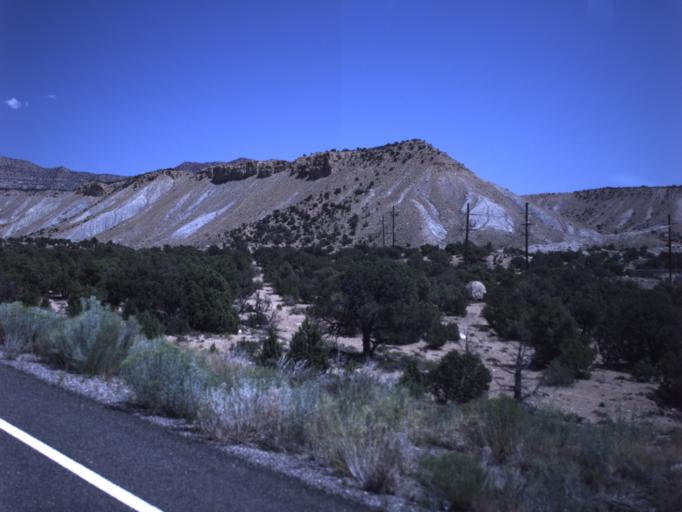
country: US
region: Utah
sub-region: Emery County
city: Orangeville
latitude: 39.2741
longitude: -111.1013
